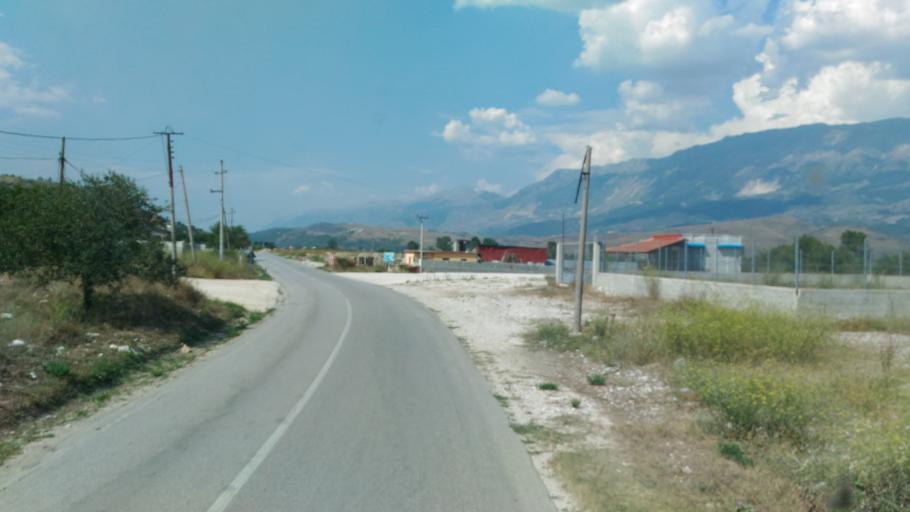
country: AL
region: Gjirokaster
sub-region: Rrethi i Gjirokastres
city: Dervician
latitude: 40.0520
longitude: 20.1775
